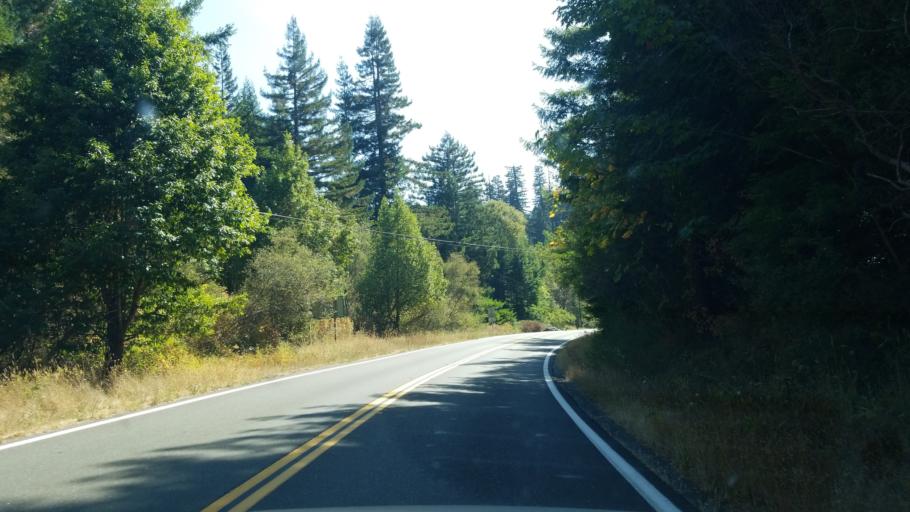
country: US
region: California
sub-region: Humboldt County
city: Redway
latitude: 40.3271
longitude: -123.9255
